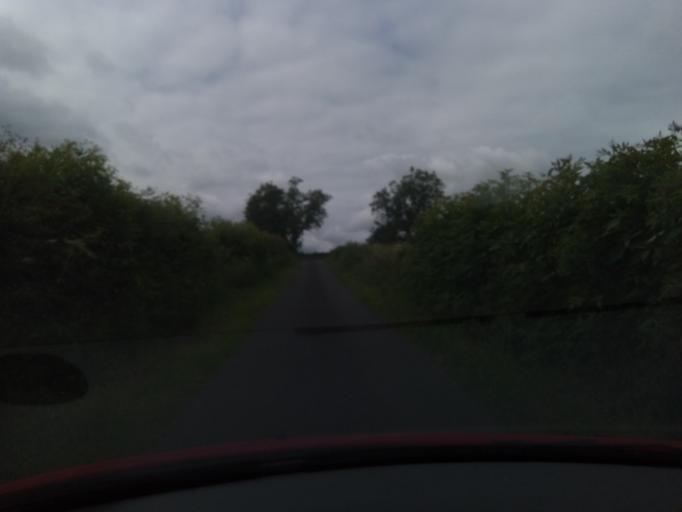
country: GB
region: Scotland
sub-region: The Scottish Borders
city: Hawick
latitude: 55.4556
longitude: -2.7437
